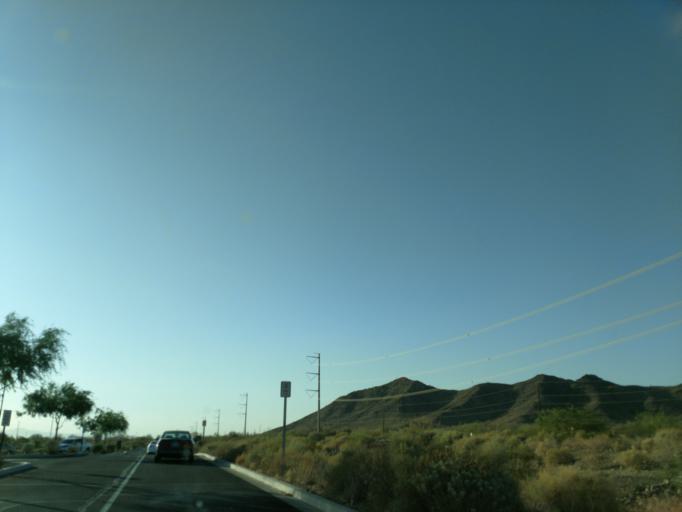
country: US
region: Arizona
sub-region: Maricopa County
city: Laveen
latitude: 33.3102
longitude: -112.1547
